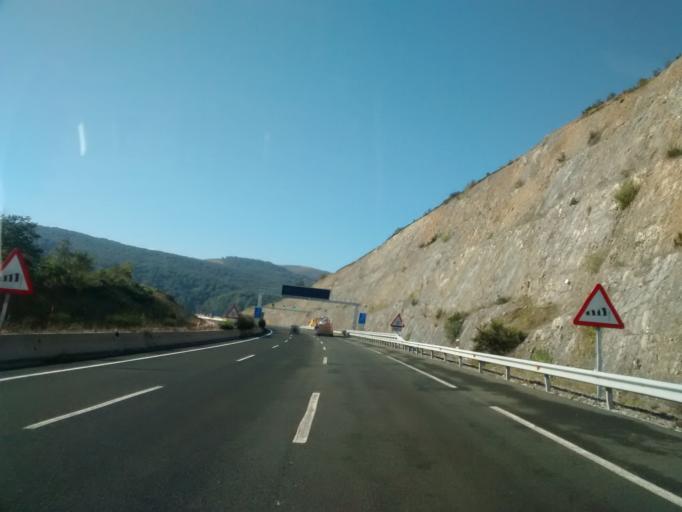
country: ES
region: Cantabria
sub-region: Provincia de Cantabria
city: Pesquera
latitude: 43.1112
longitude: -4.0872
